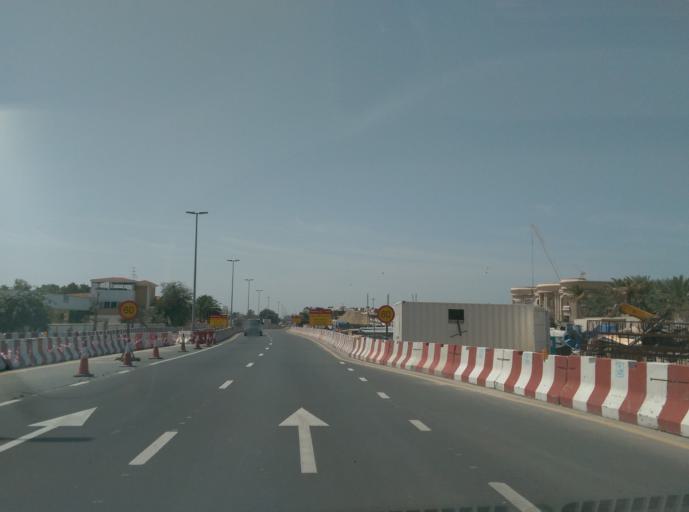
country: AE
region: Dubai
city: Dubai
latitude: 25.1935
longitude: 55.2446
